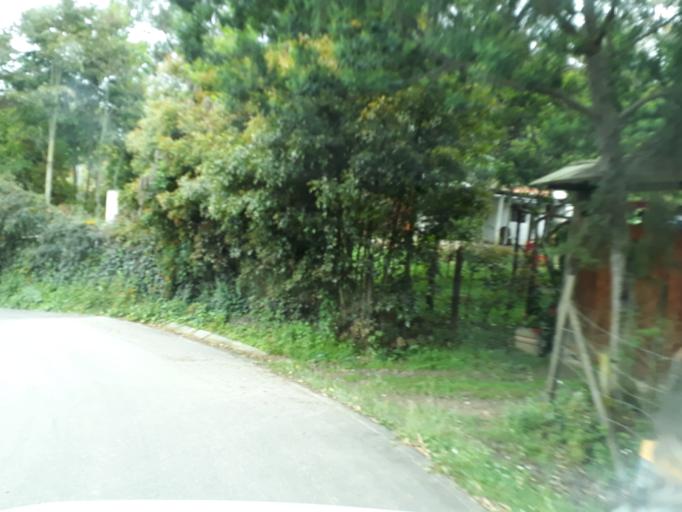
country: CO
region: Cundinamarca
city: Junin
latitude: 4.8142
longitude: -73.6719
